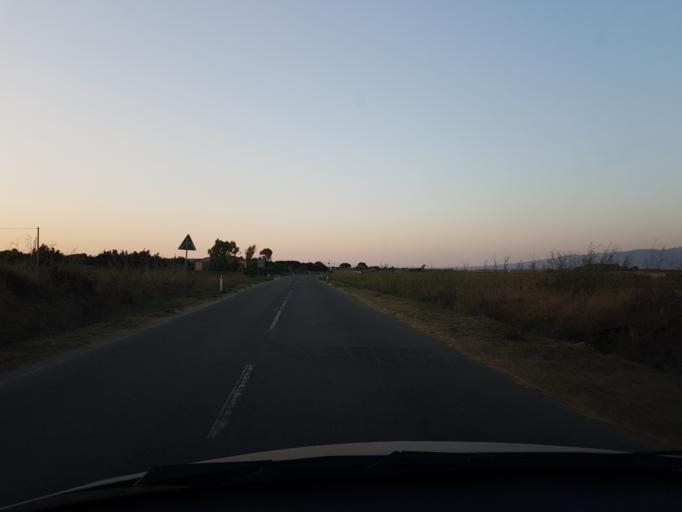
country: IT
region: Sardinia
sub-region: Provincia di Oristano
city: Nurachi
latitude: 39.9798
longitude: 8.4542
